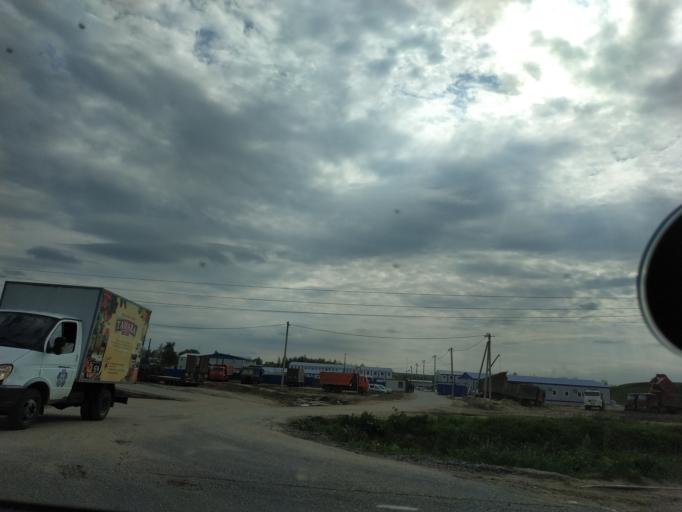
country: RU
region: Moskovskaya
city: Malyshevo
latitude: 55.4871
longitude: 38.3238
